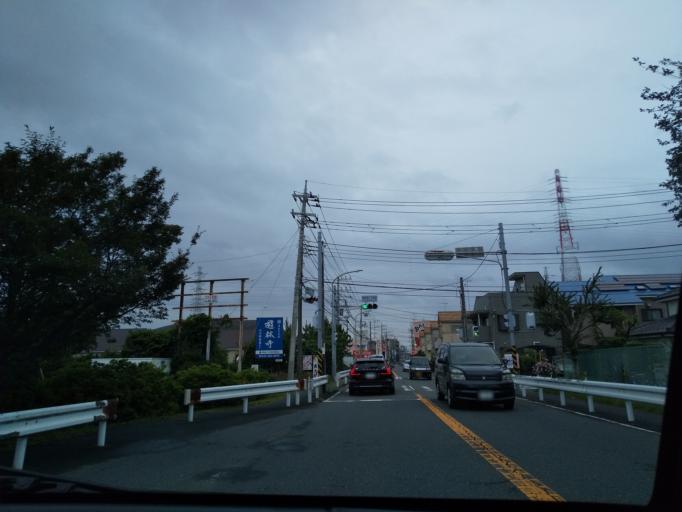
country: JP
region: Kanagawa
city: Fujisawa
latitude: 35.4019
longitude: 139.5018
